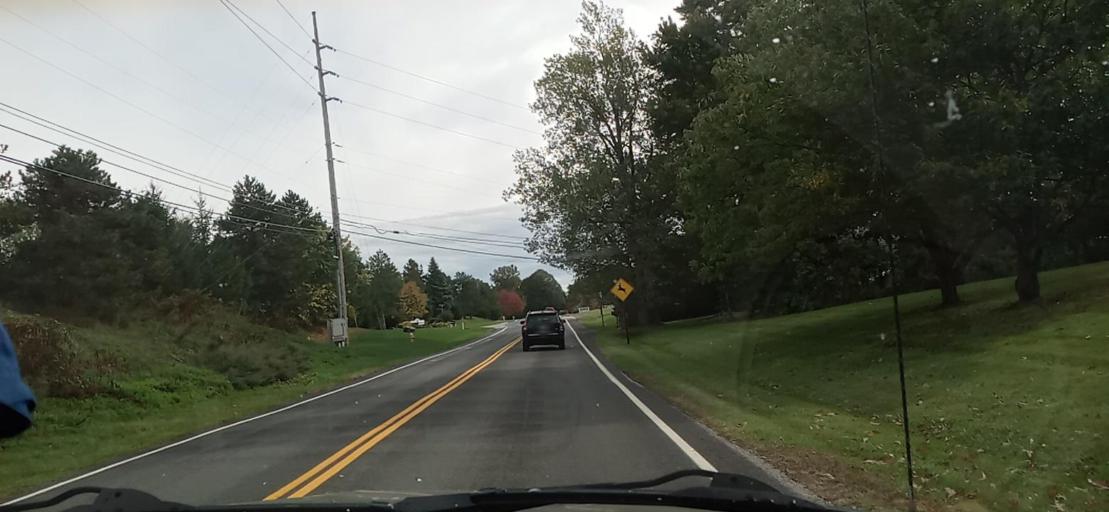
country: US
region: Ohio
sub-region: Summit County
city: Portage Lakes
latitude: 41.0195
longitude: -81.5116
